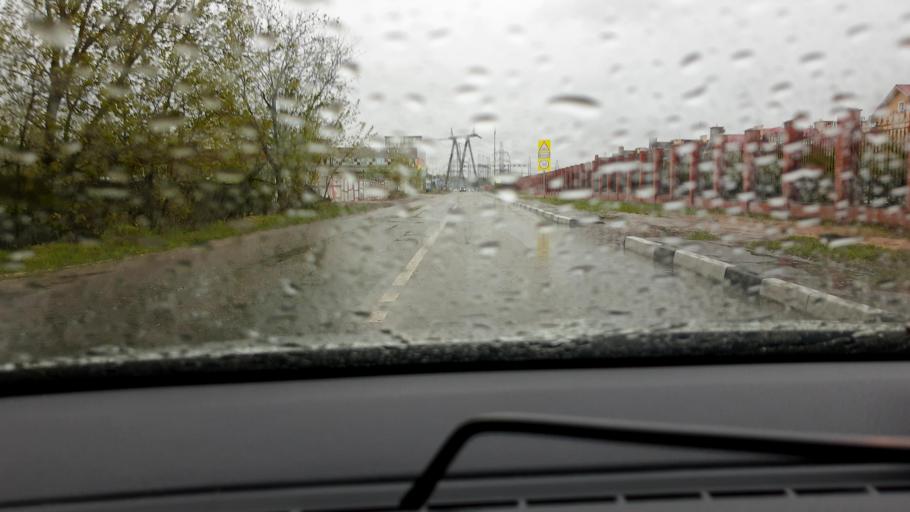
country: RU
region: Moskovskaya
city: Krasnogorsk
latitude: 55.8612
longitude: 37.3209
